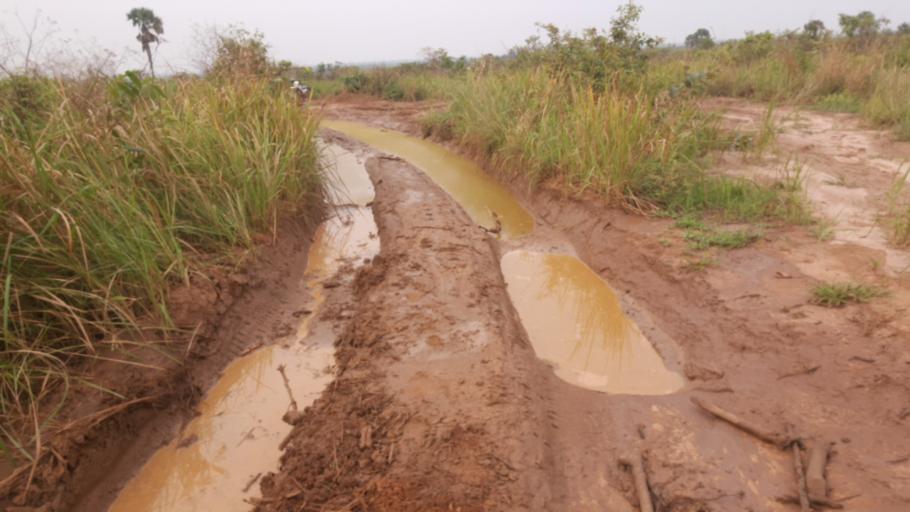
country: CD
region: Bandundu
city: Bandundu
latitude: -3.4675
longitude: 17.7138
